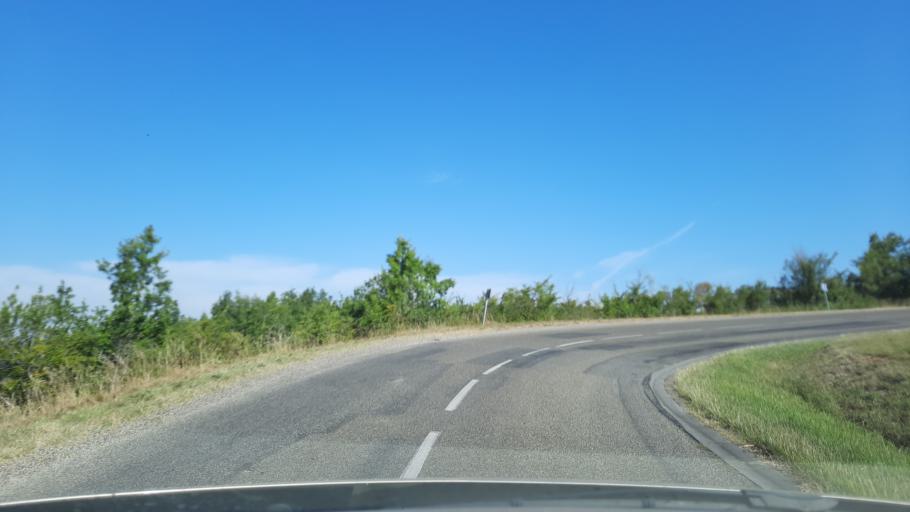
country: FR
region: Midi-Pyrenees
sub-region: Departement du Tarn-et-Garonne
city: Realville
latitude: 44.1900
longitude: 1.4637
